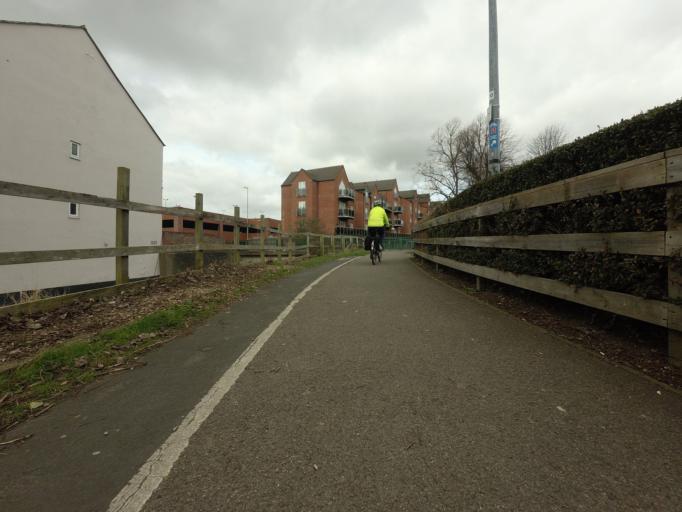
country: GB
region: England
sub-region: Lincolnshire
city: Grantham
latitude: 52.9102
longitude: -0.6367
